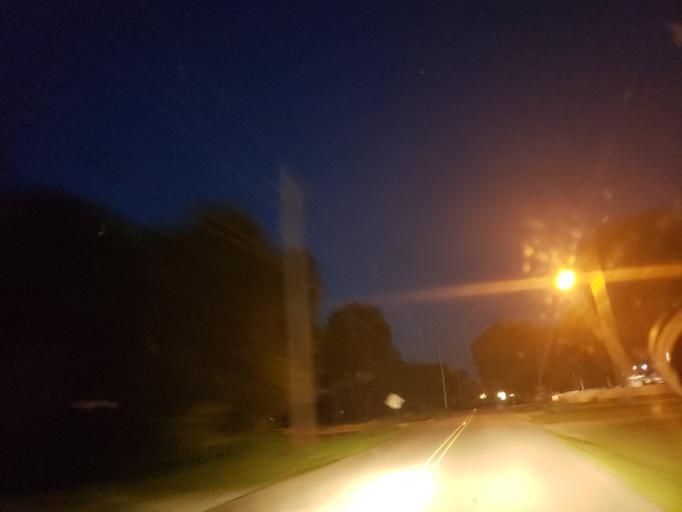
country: US
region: Alabama
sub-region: Madison County
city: Hazel Green
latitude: 34.9770
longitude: -86.6494
